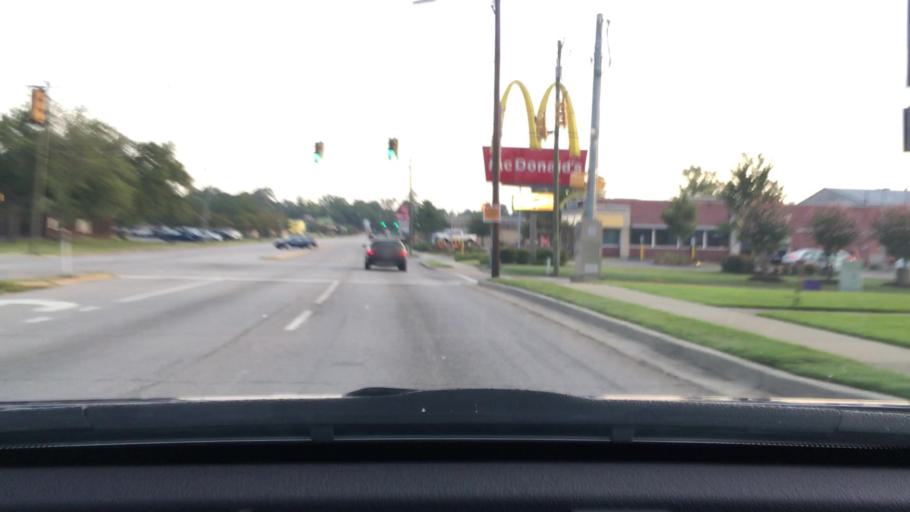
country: US
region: South Carolina
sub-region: Sumter County
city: Sumter
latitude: 33.9212
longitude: -80.3358
